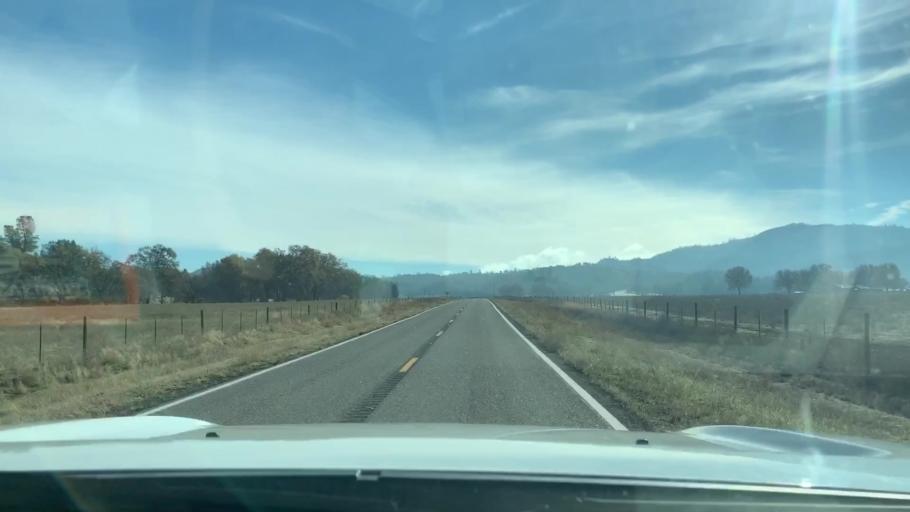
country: US
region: California
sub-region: Fresno County
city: Coalinga
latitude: 36.1801
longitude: -120.6947
